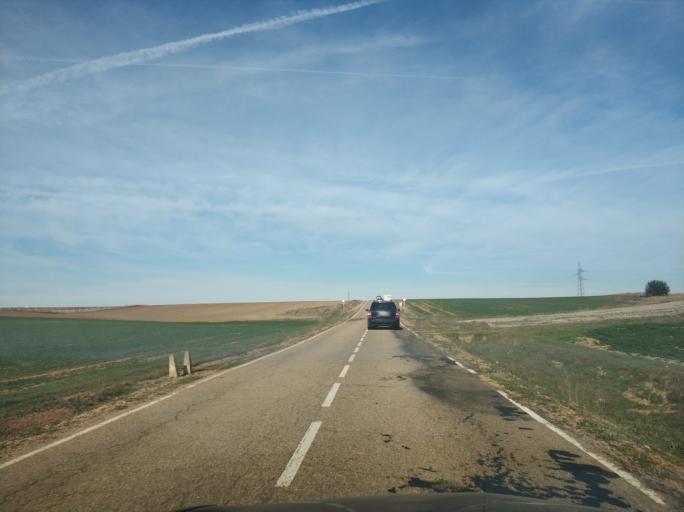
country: ES
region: Castille and Leon
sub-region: Provincia de Salamanca
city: Parada de Arriba
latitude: 40.9924
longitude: -5.8058
